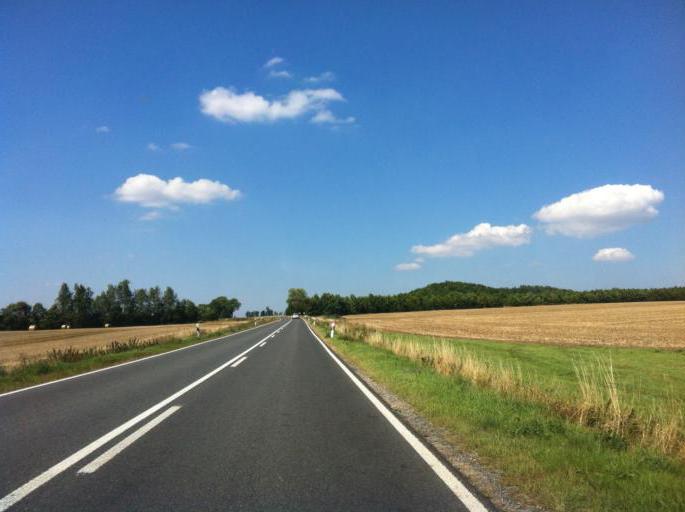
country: DE
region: Thuringia
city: Kefferhausen
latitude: 51.3308
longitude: 10.2889
